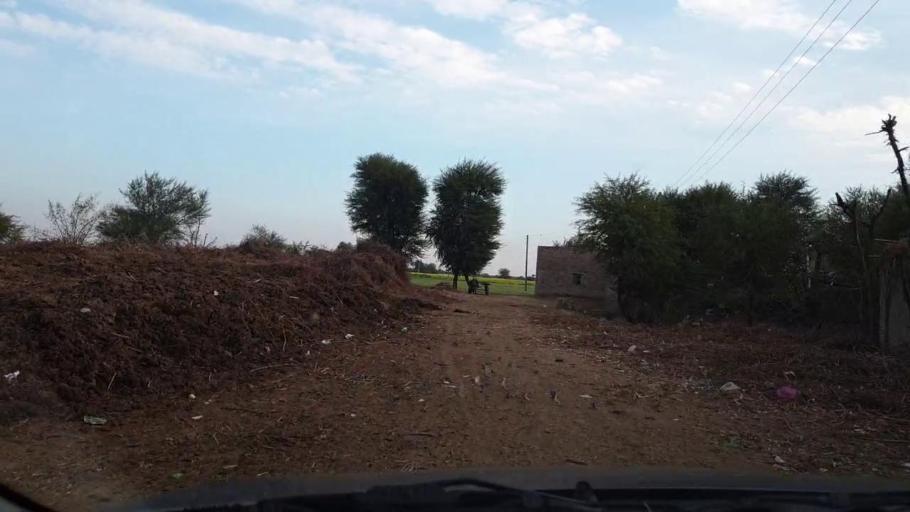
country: PK
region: Sindh
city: Jhol
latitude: 25.9802
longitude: 68.8634
